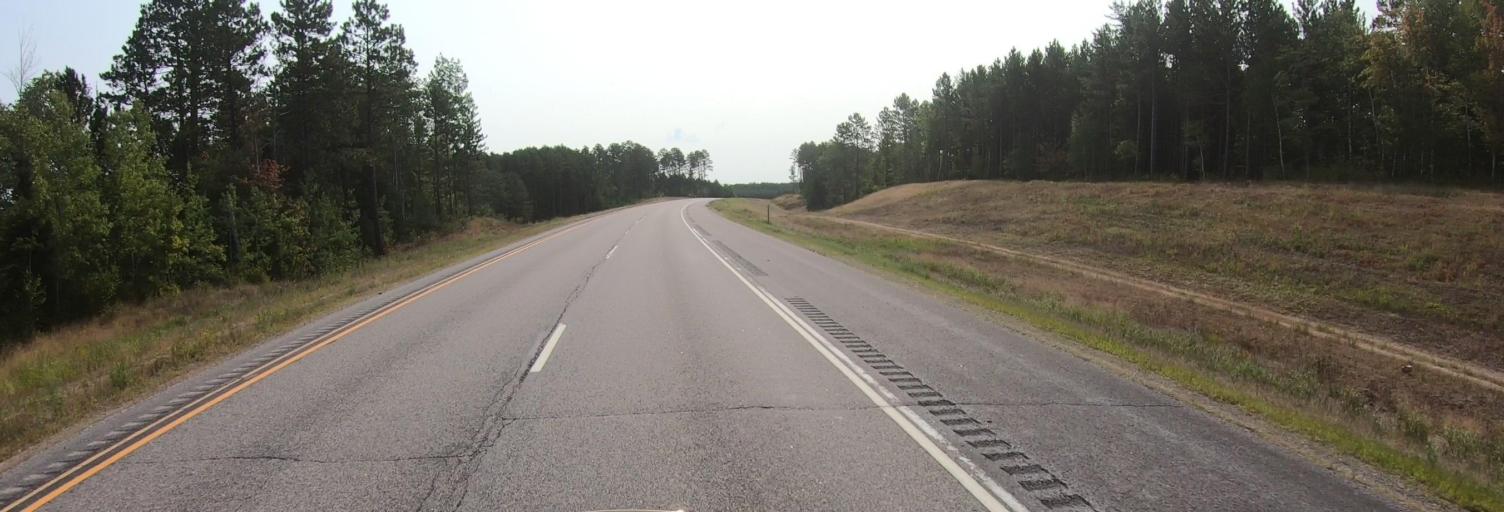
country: US
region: Minnesota
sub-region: Saint Louis County
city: Parkville
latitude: 47.6616
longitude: -92.5876
